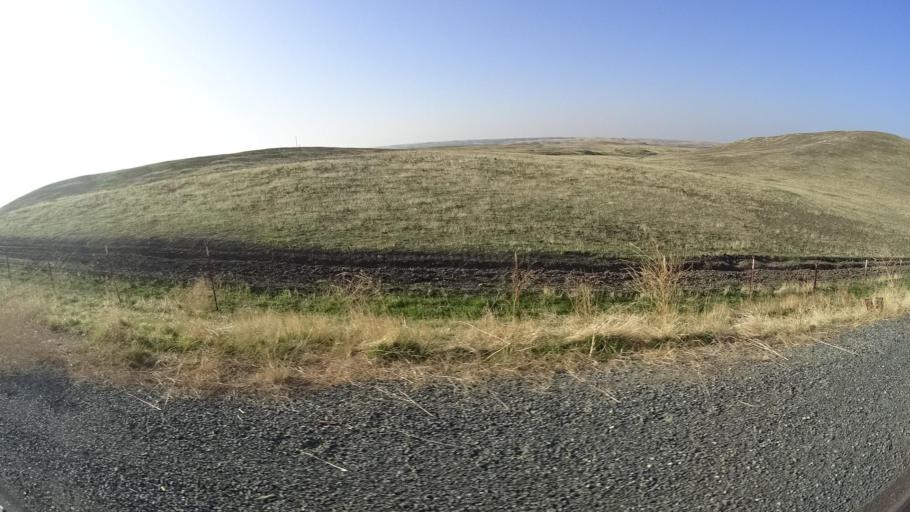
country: US
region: California
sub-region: Tulare County
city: Richgrove
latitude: 35.7455
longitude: -118.9213
